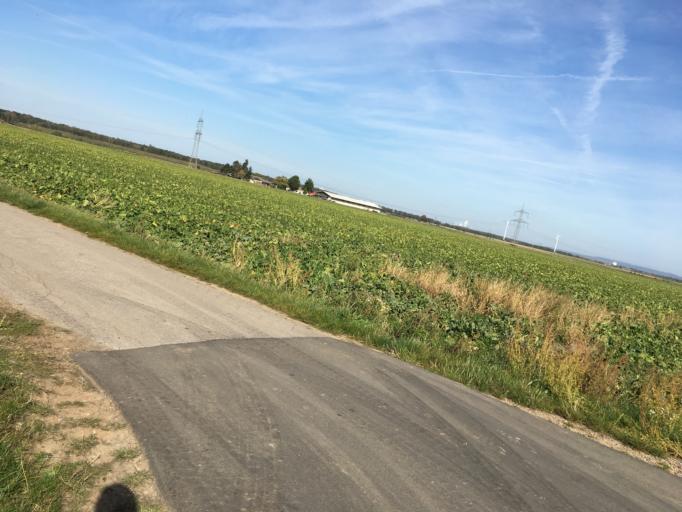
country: DE
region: North Rhine-Westphalia
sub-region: Regierungsbezirk Koln
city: Merzenich
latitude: 50.8343
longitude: 6.5366
